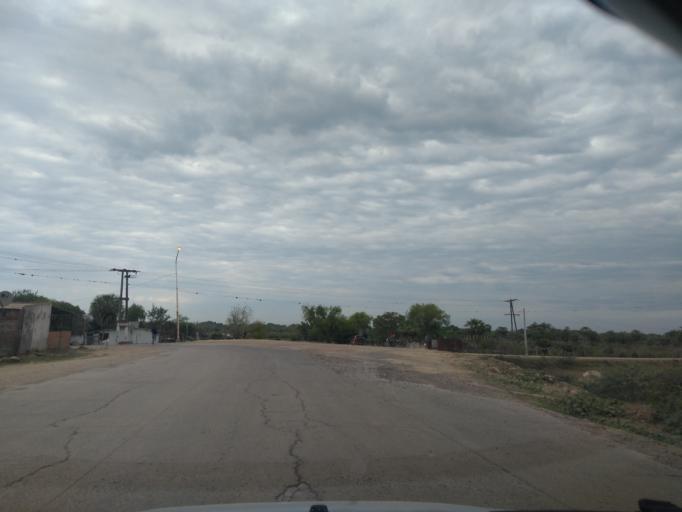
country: AR
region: Chaco
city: Puerto Vilelas
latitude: -27.5355
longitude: -58.9242
